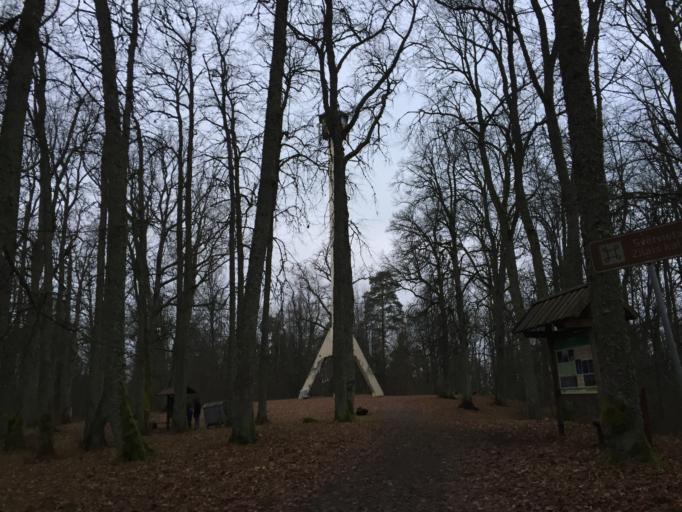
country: LV
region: Koceni
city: Koceni
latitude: 57.5532
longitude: 25.2173
